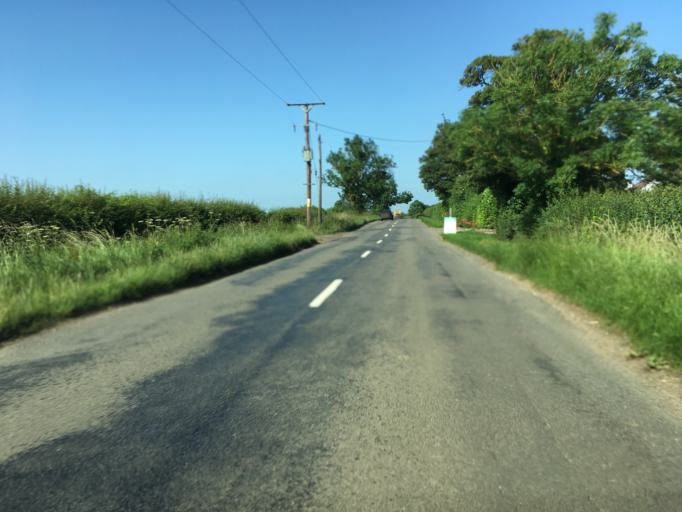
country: GB
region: England
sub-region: Buckinghamshire
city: Newton Longville
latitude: 51.9588
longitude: -0.7552
